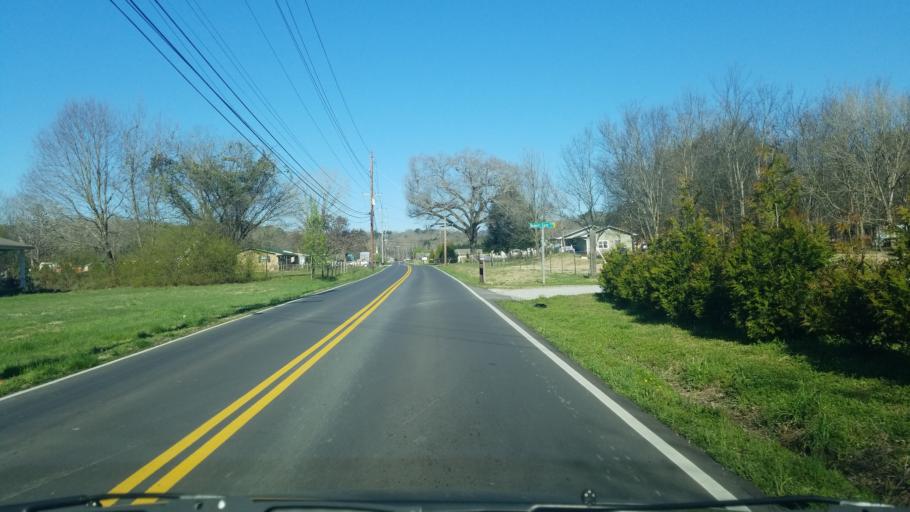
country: US
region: Tennessee
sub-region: Hamilton County
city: Middle Valley
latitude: 35.2040
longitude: -85.1618
